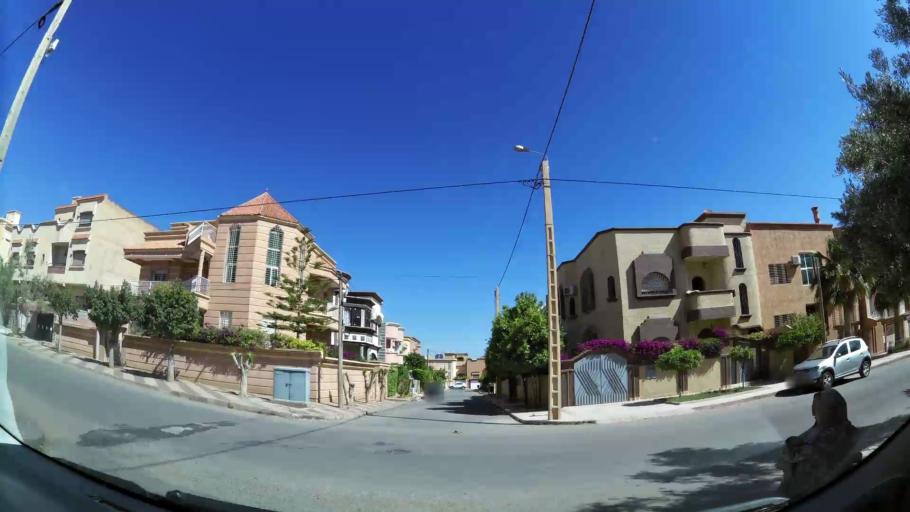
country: MA
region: Oriental
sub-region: Oujda-Angad
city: Oujda
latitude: 34.6572
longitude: -1.8871
